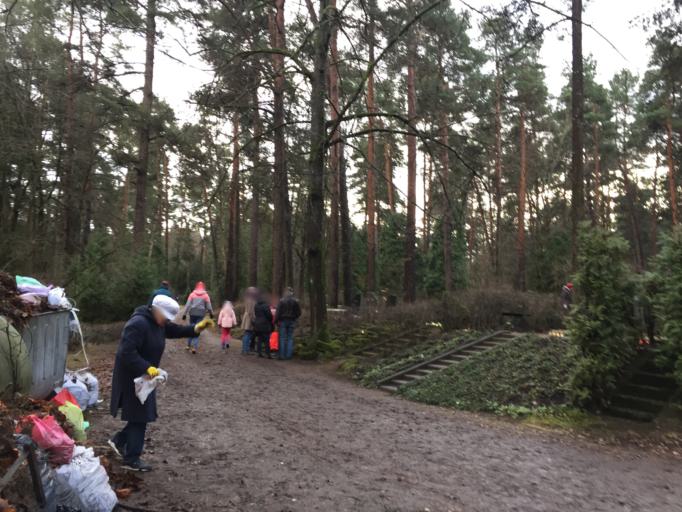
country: LV
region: Riga
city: Jaunciems
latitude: 56.9926
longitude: 24.1441
